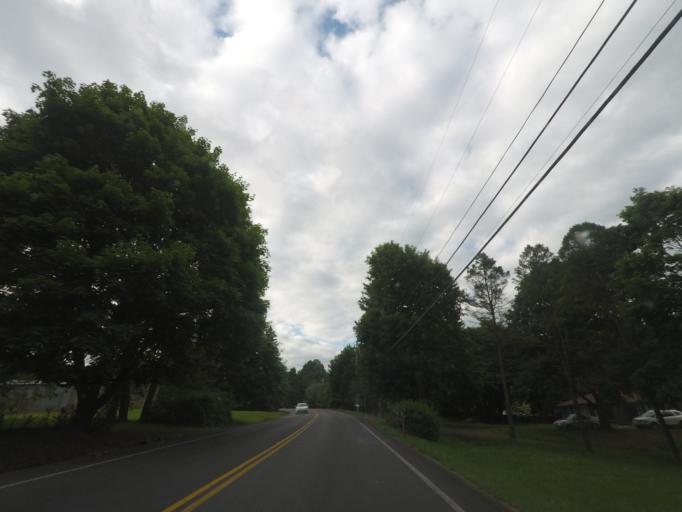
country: US
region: New York
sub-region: Orange County
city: Orange Lake
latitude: 41.5812
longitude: -74.1162
